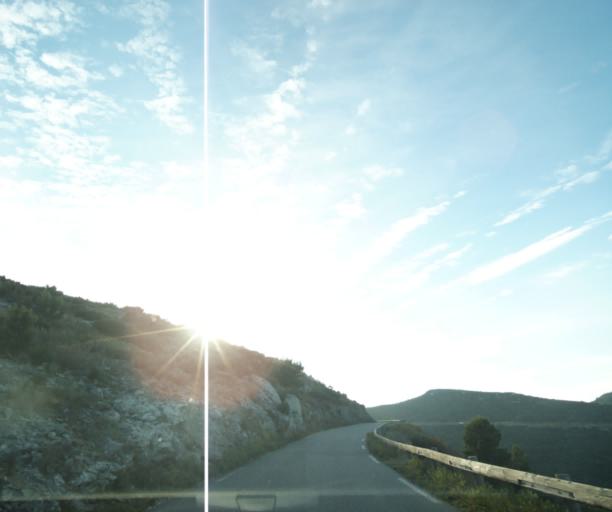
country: FR
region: Provence-Alpes-Cote d'Azur
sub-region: Departement des Bouches-du-Rhone
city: Cassis
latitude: 43.1901
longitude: 5.5634
